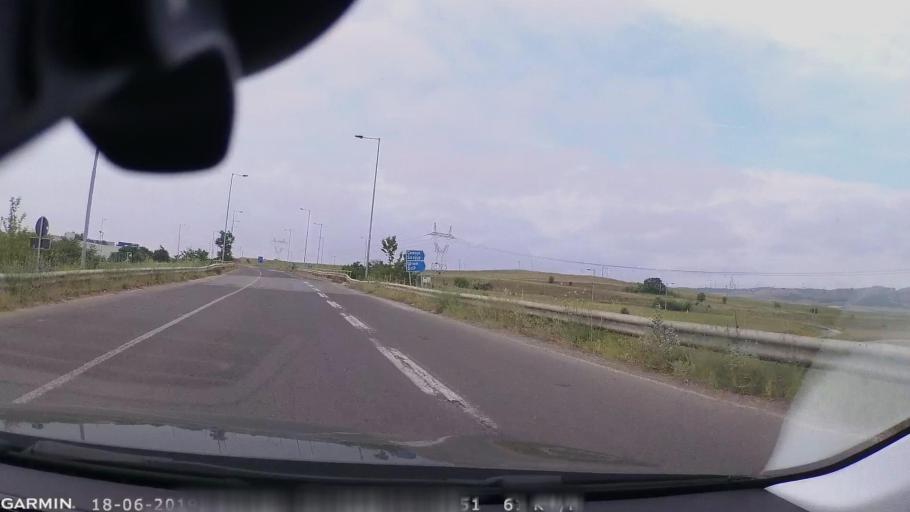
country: MK
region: Stip
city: Shtip
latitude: 41.7646
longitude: 22.1621
